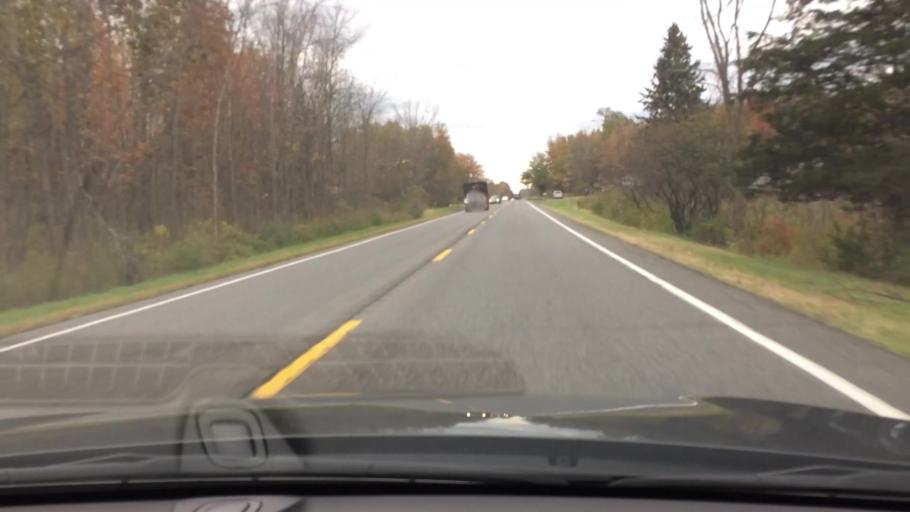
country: US
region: New York
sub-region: Columbia County
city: Kinderhook
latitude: 42.3610
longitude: -73.7054
